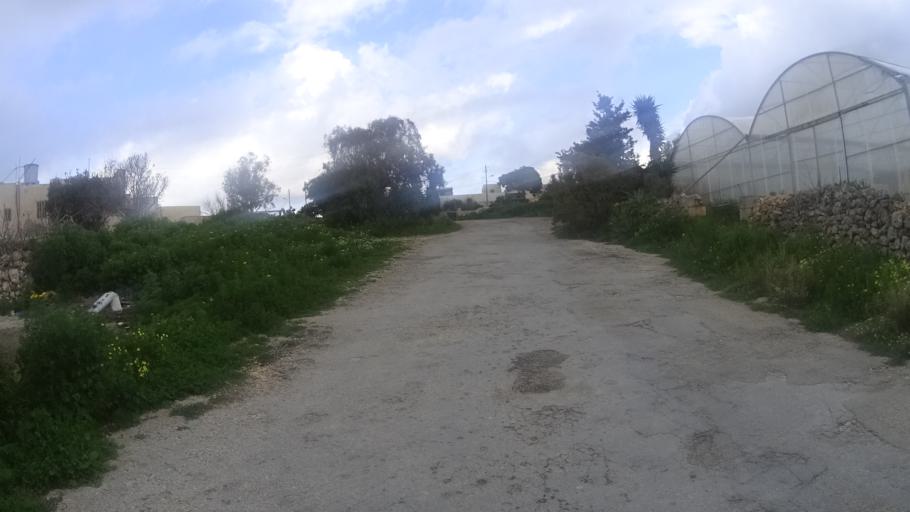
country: MT
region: L-Imgarr
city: Imgarr
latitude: 35.8969
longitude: 14.3657
